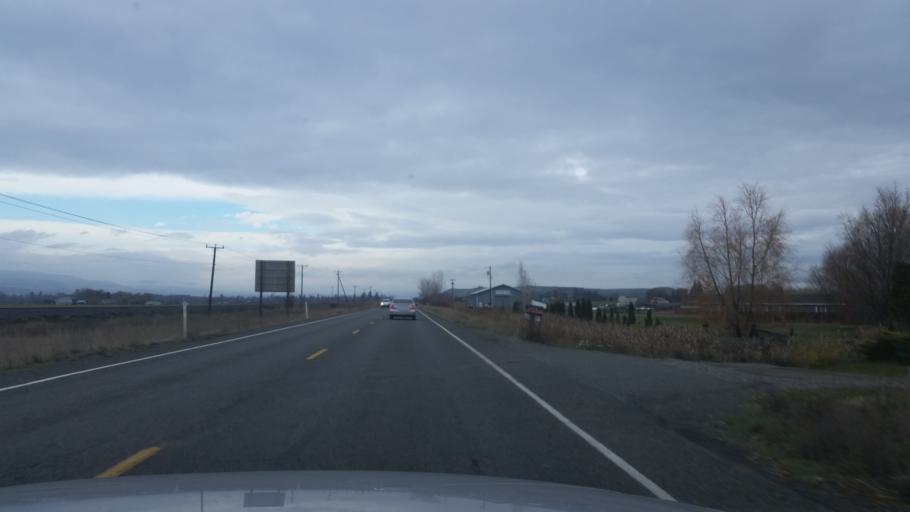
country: US
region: Washington
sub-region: Kittitas County
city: Ellensburg
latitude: 47.0255
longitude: -120.5977
